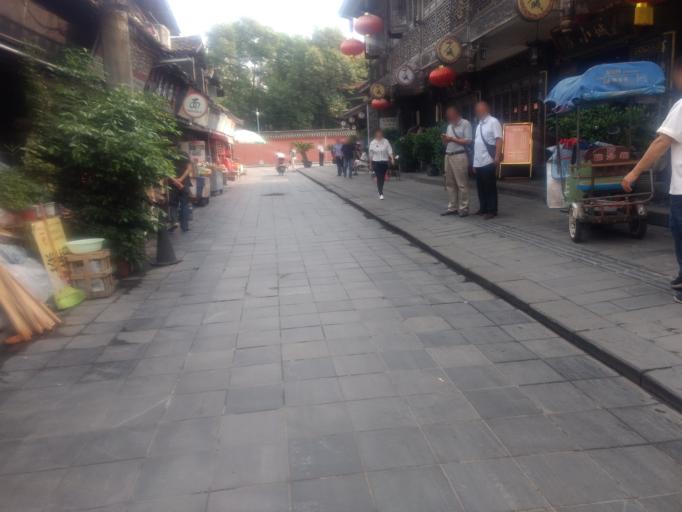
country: CN
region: Sichuan
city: Chengdu
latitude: 30.6763
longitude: 104.0699
